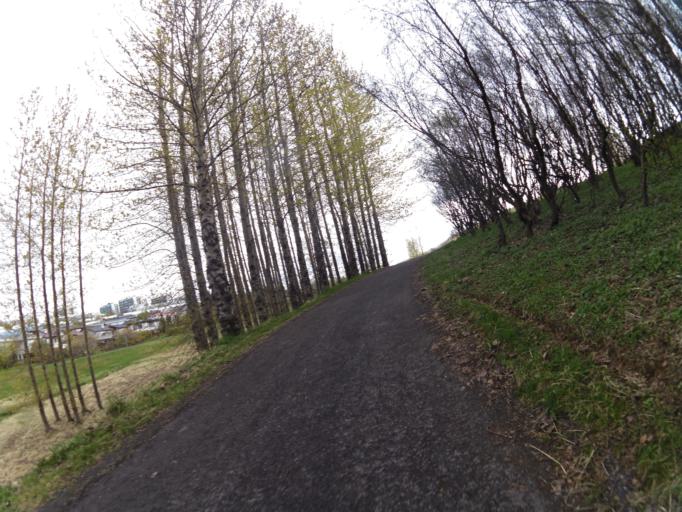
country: IS
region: Capital Region
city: Reykjavik
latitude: 64.1071
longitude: -21.8672
